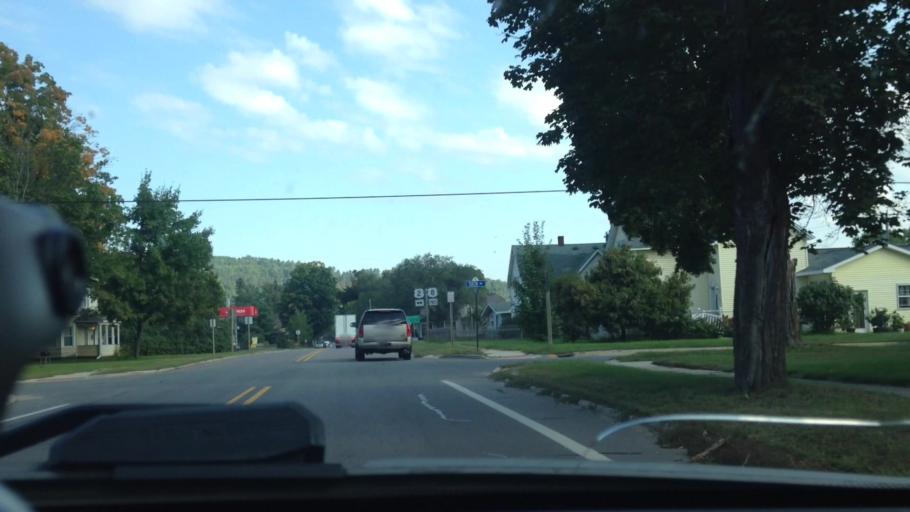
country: US
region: Michigan
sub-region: Dickinson County
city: Norway
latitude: 45.7858
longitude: -87.9099
